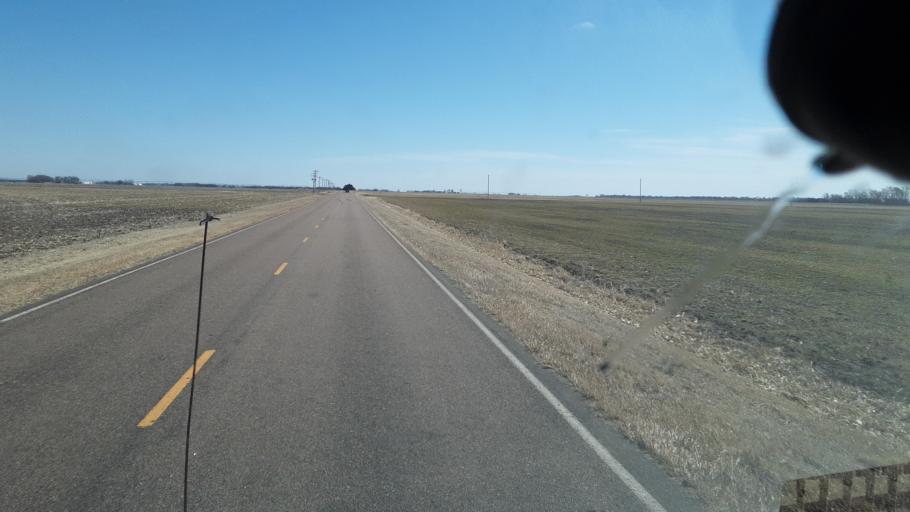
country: US
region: Kansas
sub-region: Rice County
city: Sterling
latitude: 38.2461
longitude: -98.2745
